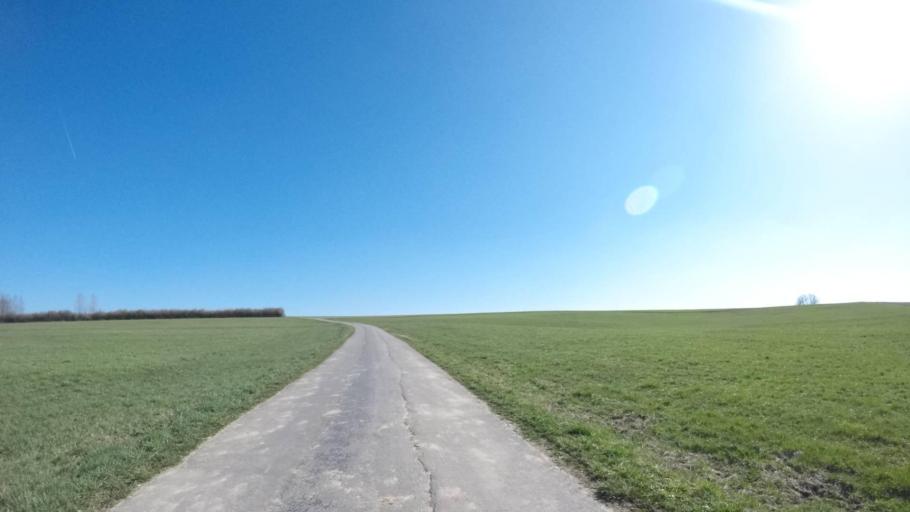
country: DE
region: Saxony
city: Niederfrohna
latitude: 50.8850
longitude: 12.6927
